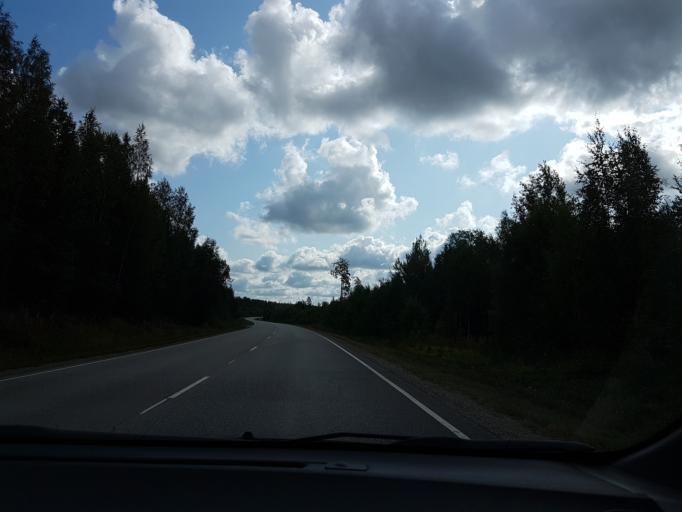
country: FI
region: Uusimaa
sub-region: Helsinki
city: Nickby
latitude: 60.4699
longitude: 25.2510
